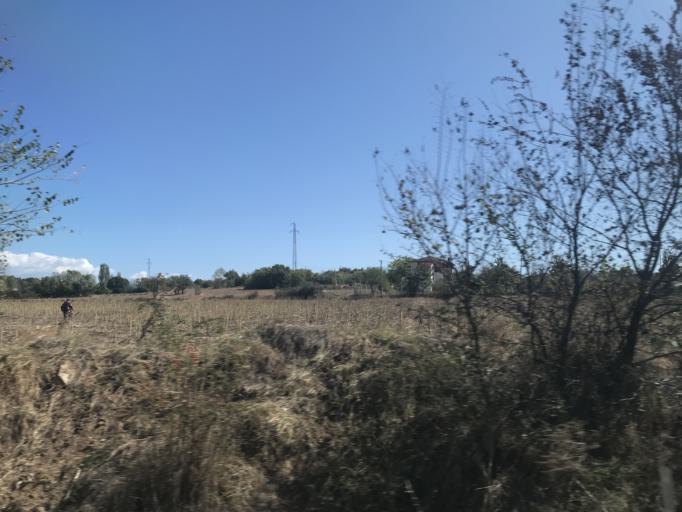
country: TR
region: Kirklareli
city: Kirklareli
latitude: 41.7775
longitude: 27.2277
